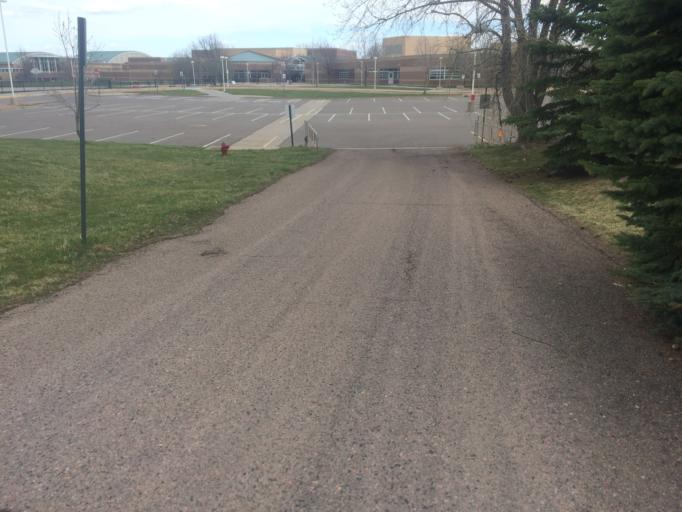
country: US
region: Colorado
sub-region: Boulder County
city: Superior
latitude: 39.9524
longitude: -105.1457
